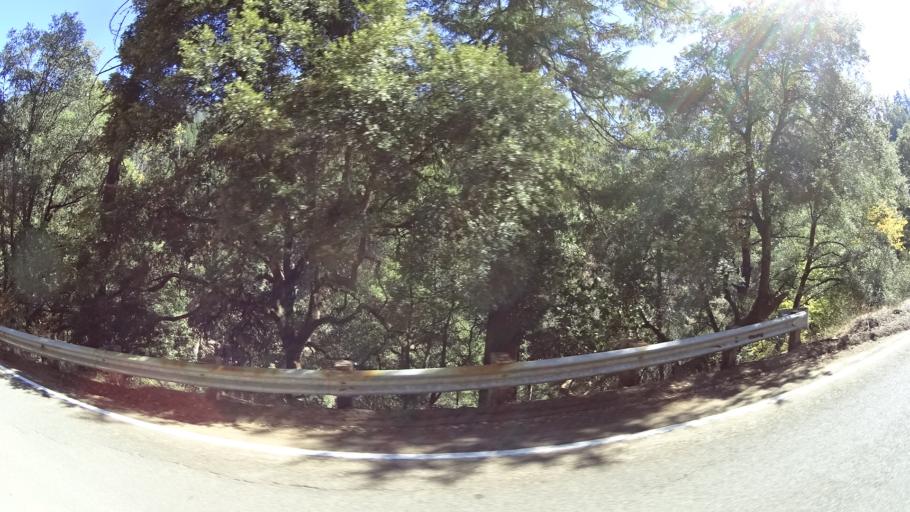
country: US
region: California
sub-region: Siskiyou County
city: Happy Camp
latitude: 41.3640
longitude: -123.4152
